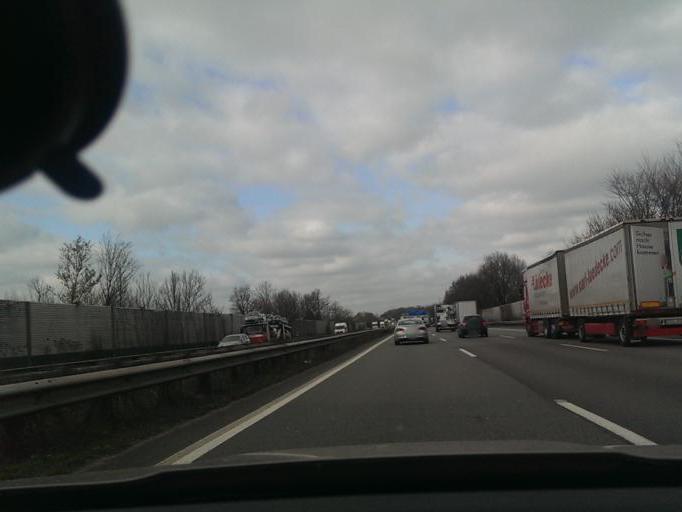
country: DE
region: North Rhine-Westphalia
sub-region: Regierungsbezirk Detmold
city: Leopoldshohe
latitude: 52.0482
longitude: 8.6544
